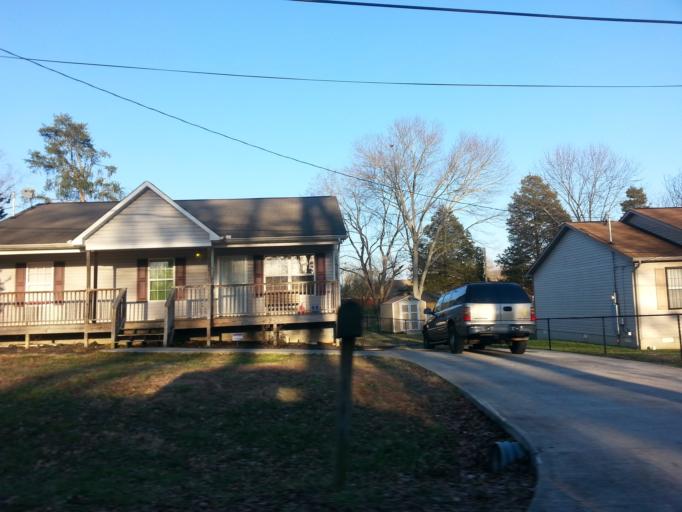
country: US
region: Tennessee
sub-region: Knox County
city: Knoxville
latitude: 36.0152
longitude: -83.9018
